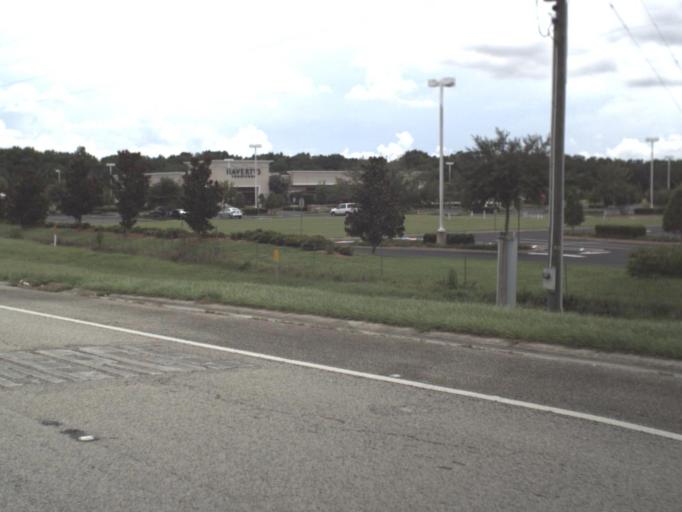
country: US
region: Florida
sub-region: Hillsborough County
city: Pebble Creek
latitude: 28.1923
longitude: -82.3809
